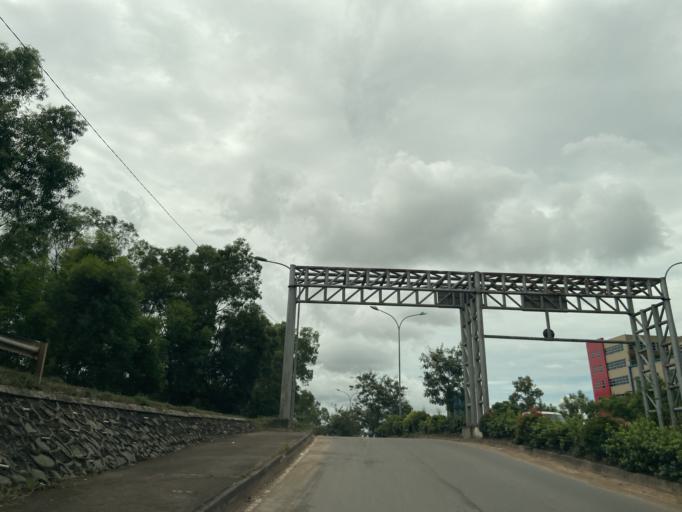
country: SG
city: Singapore
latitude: 1.1394
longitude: 104.0238
